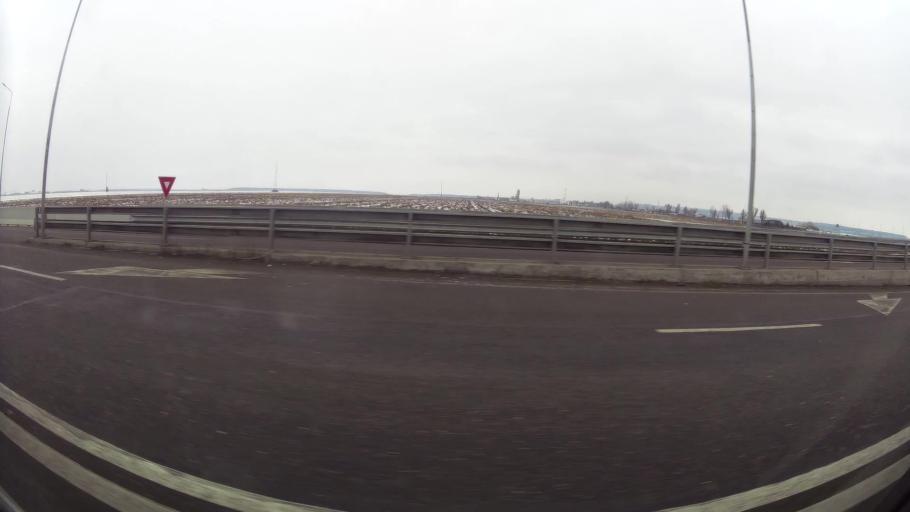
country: RO
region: Prahova
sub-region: Comuna Paulesti
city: Paulesti
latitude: 44.9757
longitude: 25.9903
